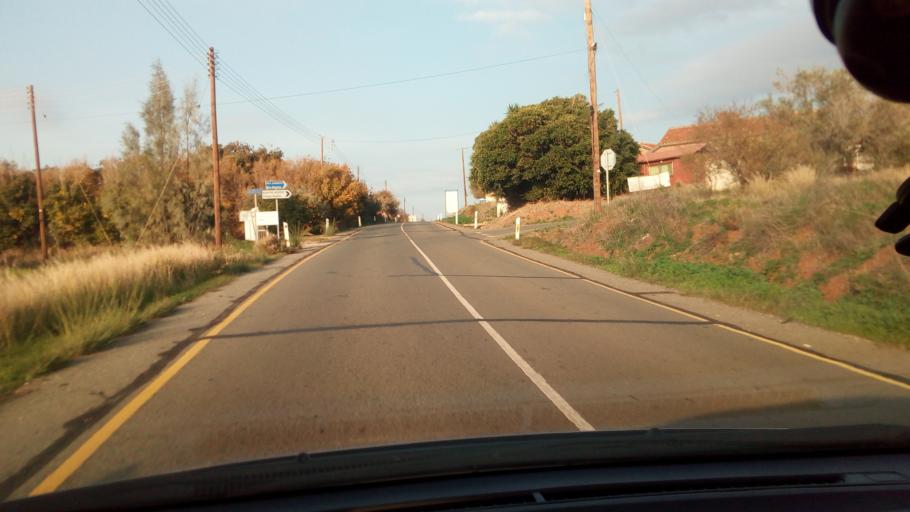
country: CY
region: Pafos
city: Polis
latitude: 35.1346
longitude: 32.5204
